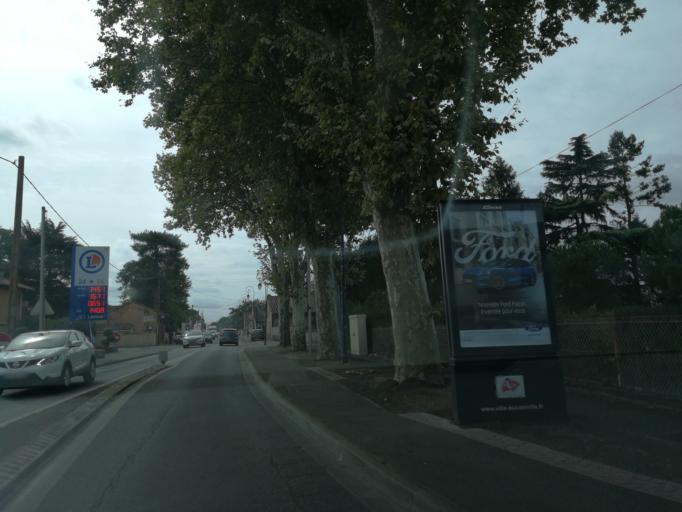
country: FR
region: Midi-Pyrenees
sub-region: Departement de la Haute-Garonne
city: Aucamville
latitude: 43.6783
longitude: 1.4230
